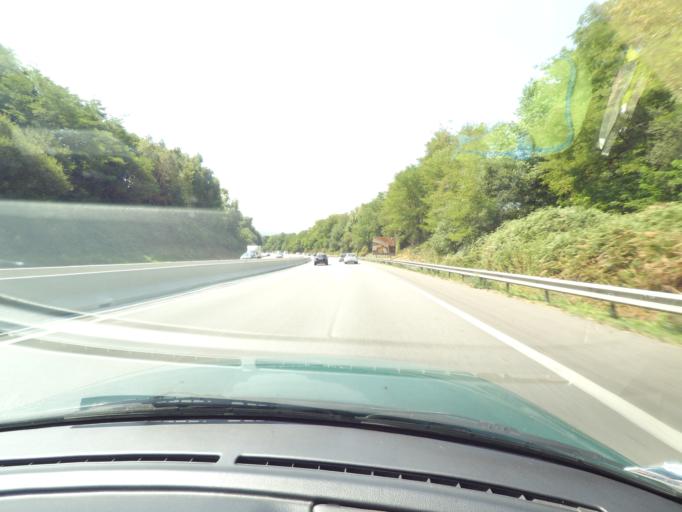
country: FR
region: Limousin
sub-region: Departement de la Haute-Vienne
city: Limoges
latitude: 45.8542
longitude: 1.2769
